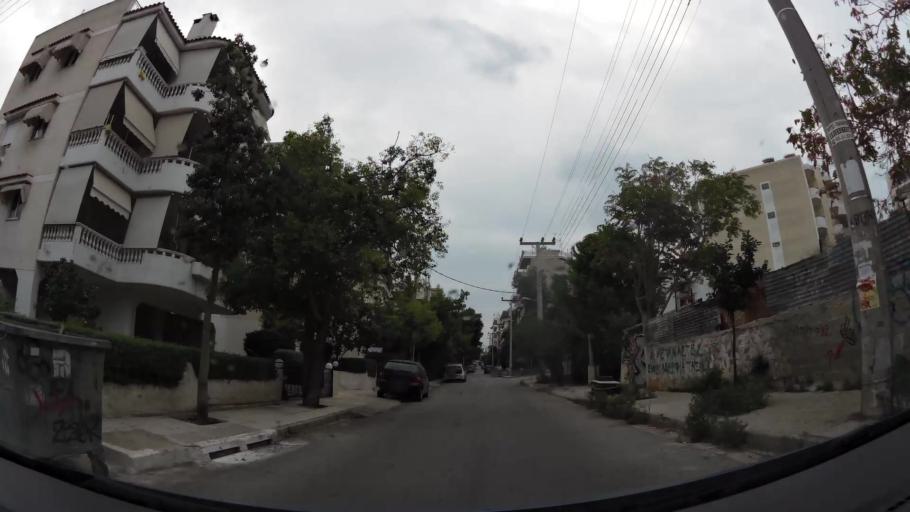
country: GR
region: Attica
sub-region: Nomarchia Athinas
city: Palaio Faliro
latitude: 37.9189
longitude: 23.7118
